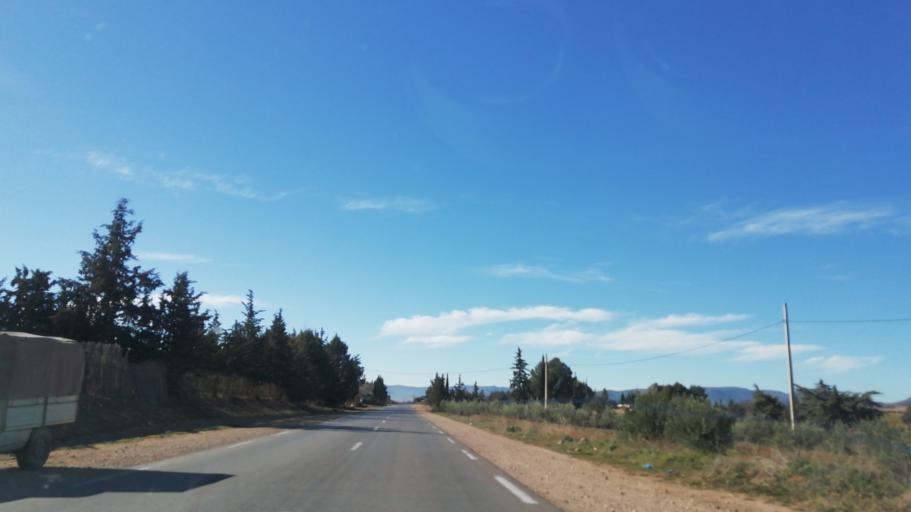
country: DZ
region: Tlemcen
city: Sebdou
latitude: 34.6819
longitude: -1.2552
